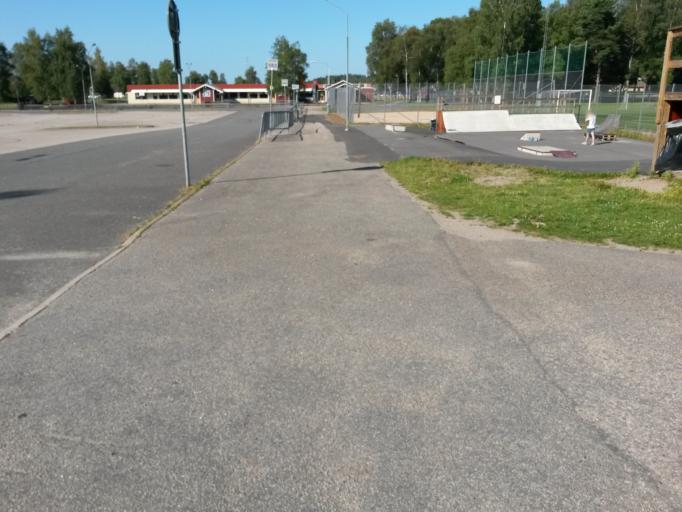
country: SE
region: Vaestra Goetaland
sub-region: Vargarda Kommun
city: Vargarda
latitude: 58.0350
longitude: 12.8231
